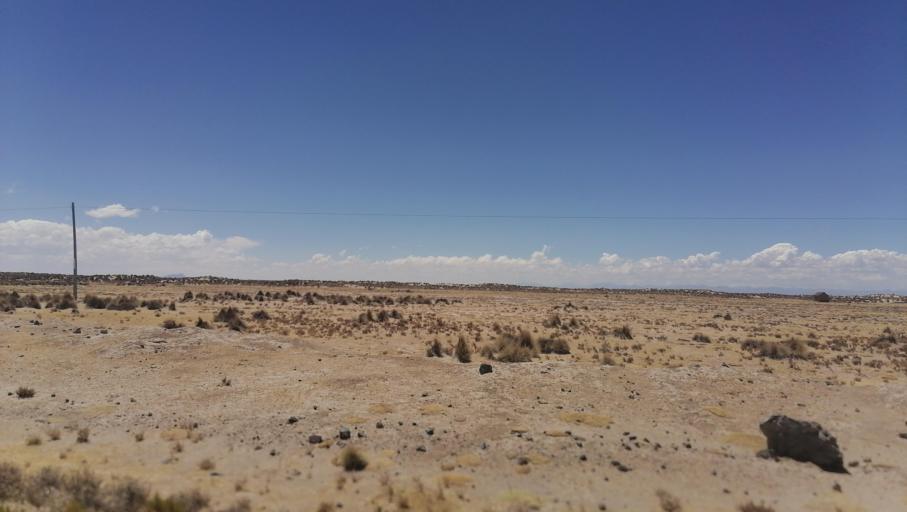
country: BO
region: Oruro
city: Challapata
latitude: -19.2222
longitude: -66.9790
